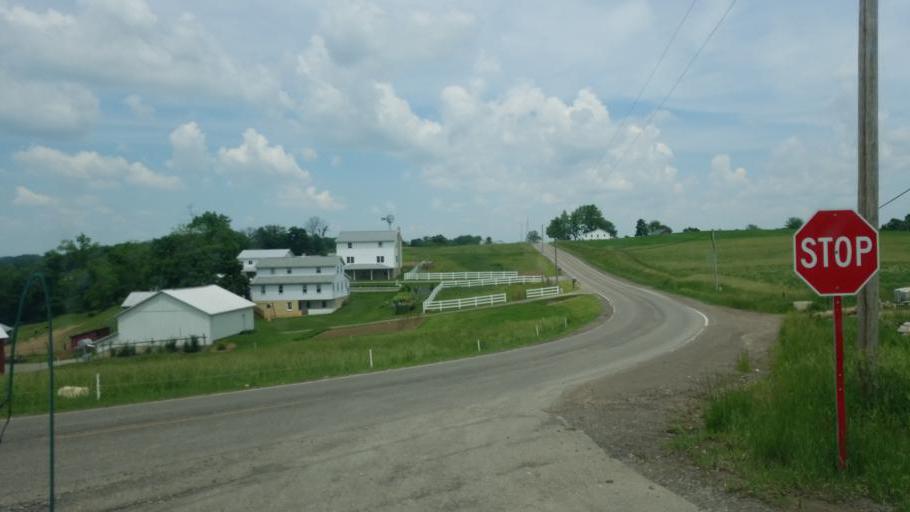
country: US
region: Ohio
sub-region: Coshocton County
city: West Lafayette
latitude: 40.4244
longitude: -81.7889
